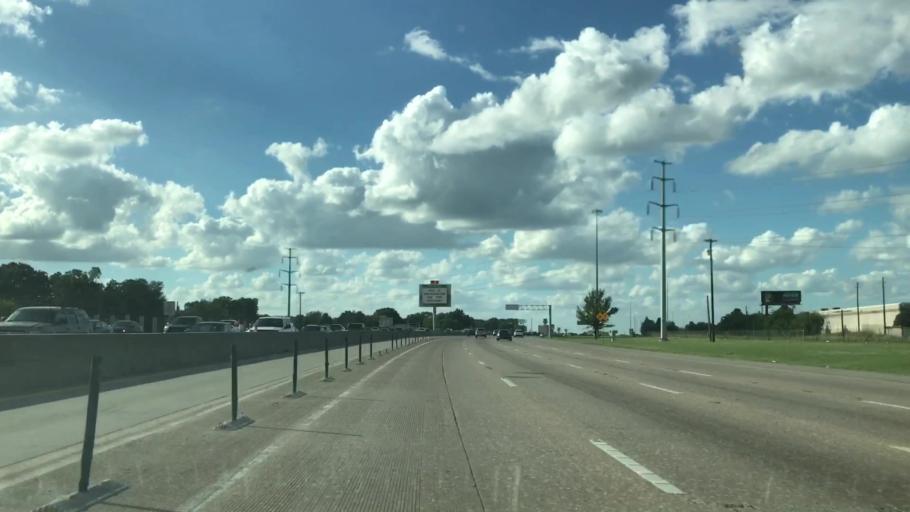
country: US
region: Texas
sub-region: Dallas County
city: Richardson
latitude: 32.8880
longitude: -96.7047
